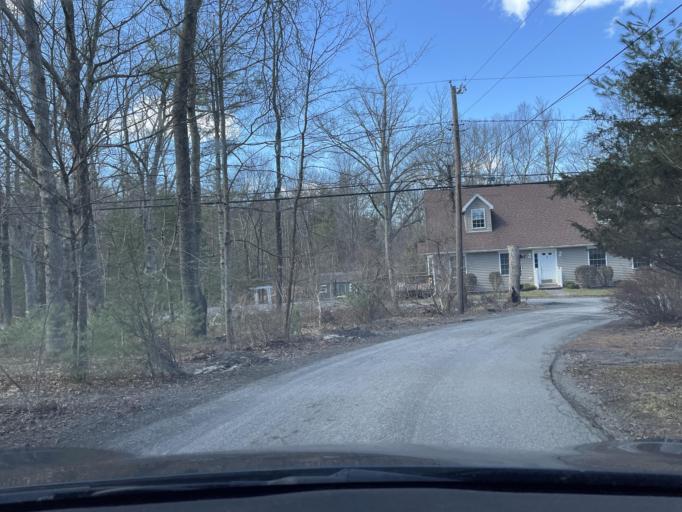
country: US
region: New York
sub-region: Ulster County
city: West Hurley
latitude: 41.9552
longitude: -74.1102
